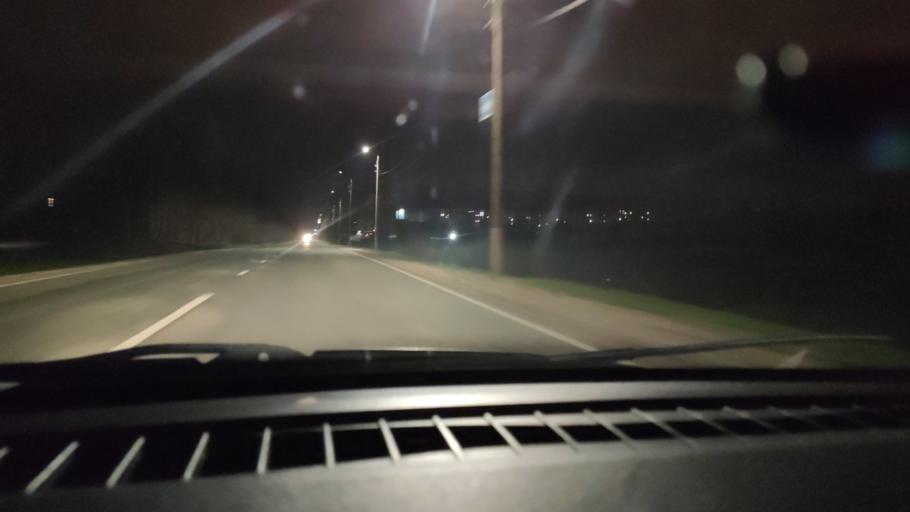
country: RU
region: Bashkortostan
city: Sterlitamak
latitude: 53.6461
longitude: 55.8856
